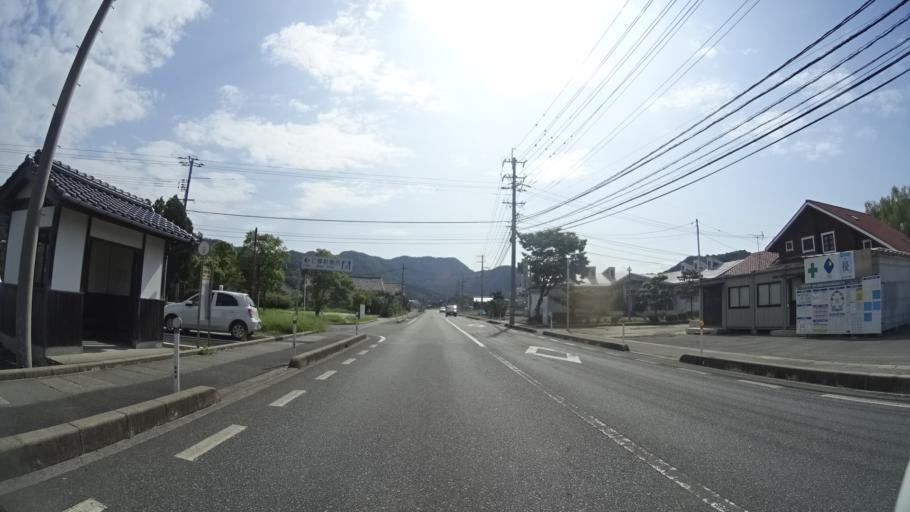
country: JP
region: Shimane
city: Odacho-oda
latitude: 35.1479
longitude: 132.4063
